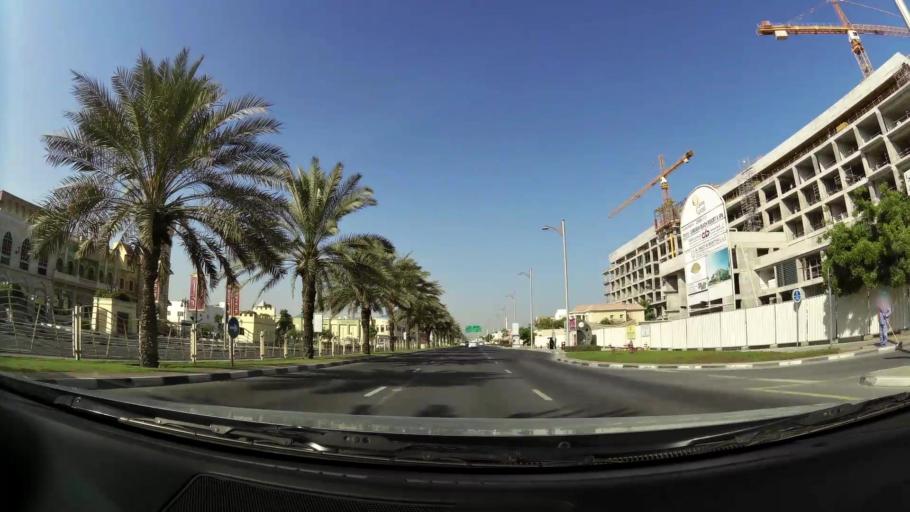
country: AE
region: Dubai
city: Dubai
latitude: 25.2171
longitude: 55.2520
